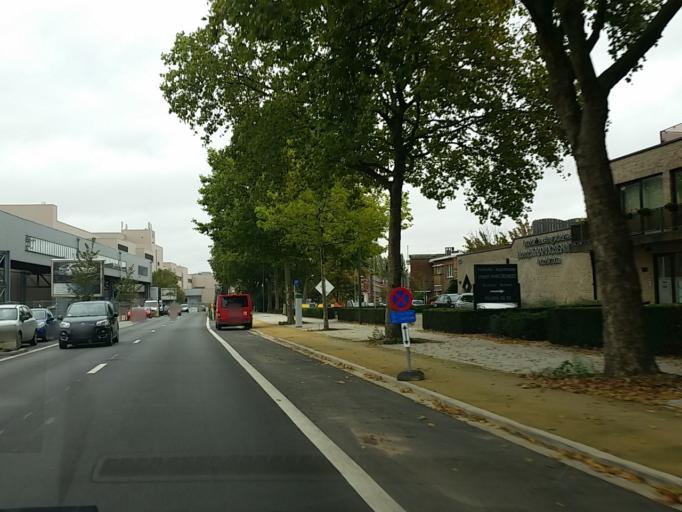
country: BE
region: Flanders
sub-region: Provincie Vlaams-Brabant
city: Drogenbos
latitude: 50.8069
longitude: 4.3120
